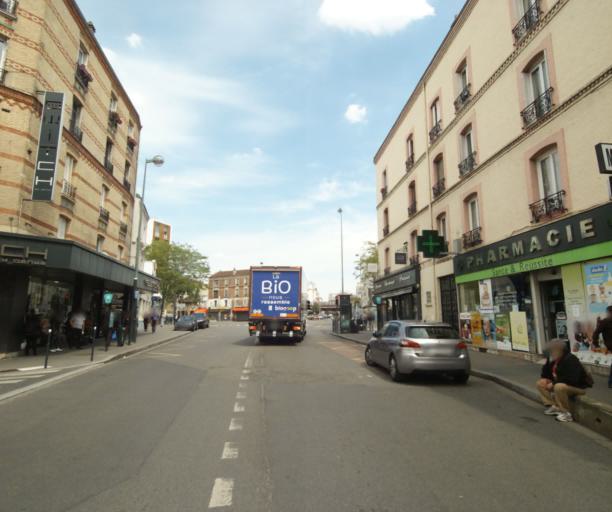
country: FR
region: Ile-de-France
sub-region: Departement des Hauts-de-Seine
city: Asnieres-sur-Seine
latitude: 48.9123
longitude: 2.2954
